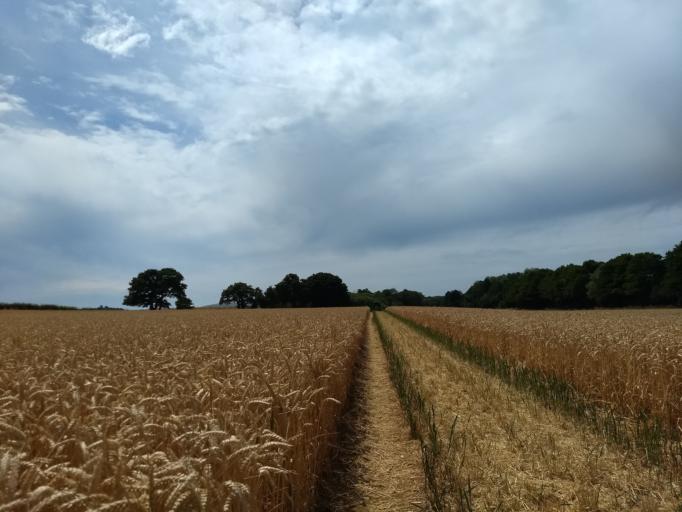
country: GB
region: England
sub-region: Isle of Wight
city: Newchurch
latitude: 50.6501
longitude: -1.2464
